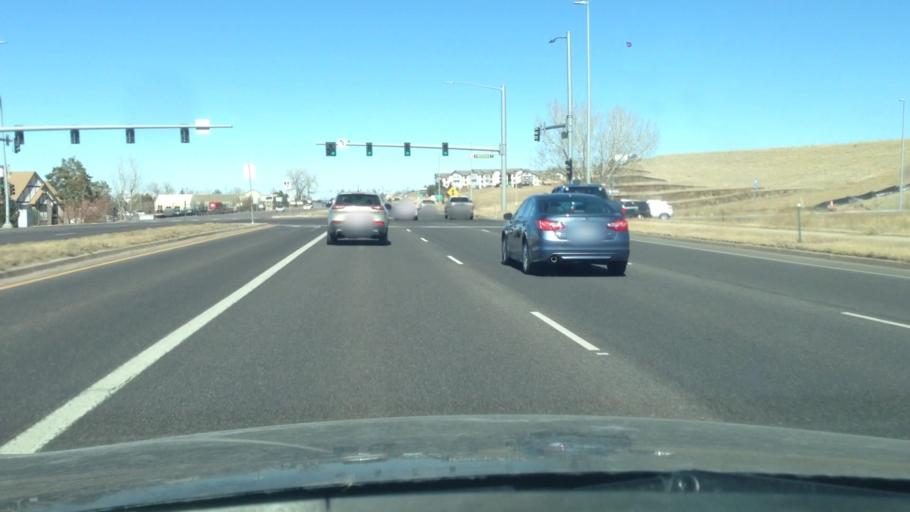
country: US
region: Colorado
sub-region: Douglas County
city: Stonegate
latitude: 39.5540
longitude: -104.7773
